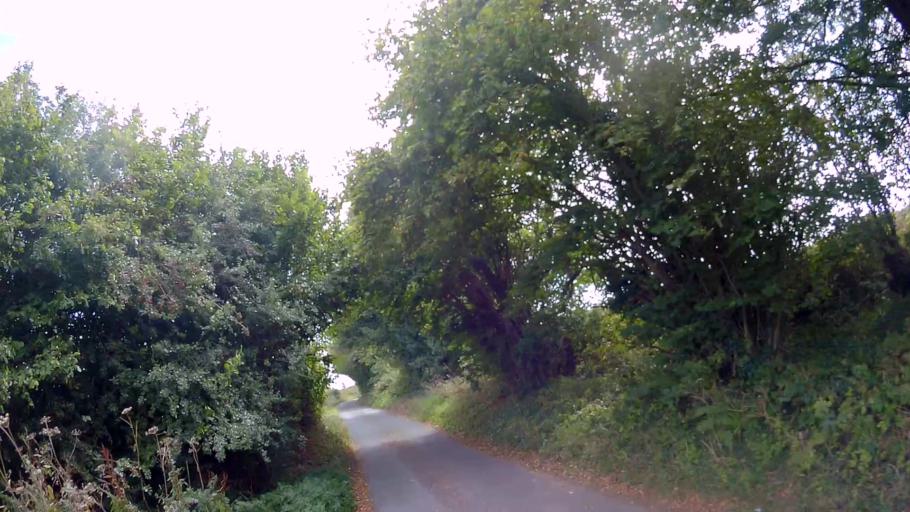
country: GB
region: England
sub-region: Hampshire
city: Odiham
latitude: 51.2418
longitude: -0.9776
